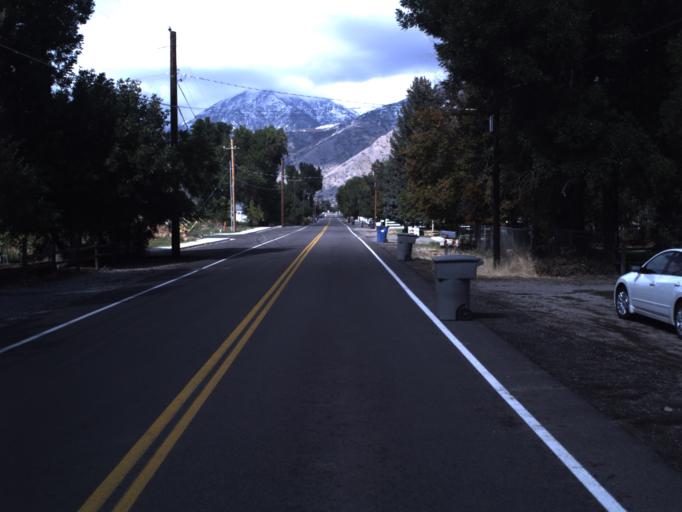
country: US
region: Utah
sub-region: Utah County
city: Mapleton
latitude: 40.1240
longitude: -111.5787
